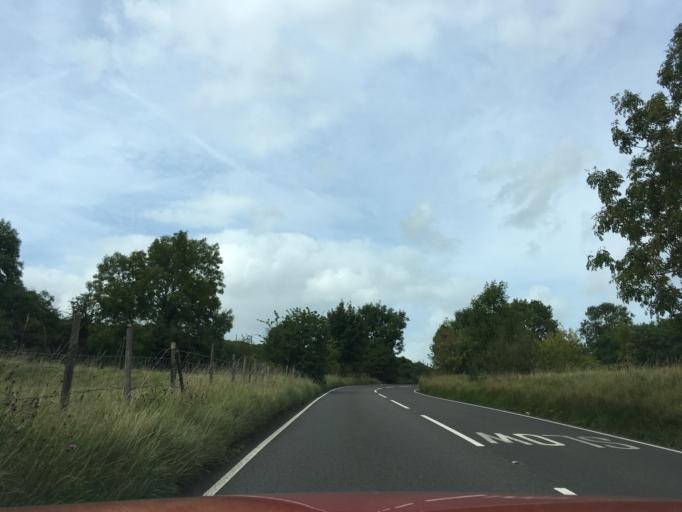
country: GB
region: England
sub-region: Gloucestershire
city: Wotton-under-Edge
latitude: 51.6475
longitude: -2.3366
